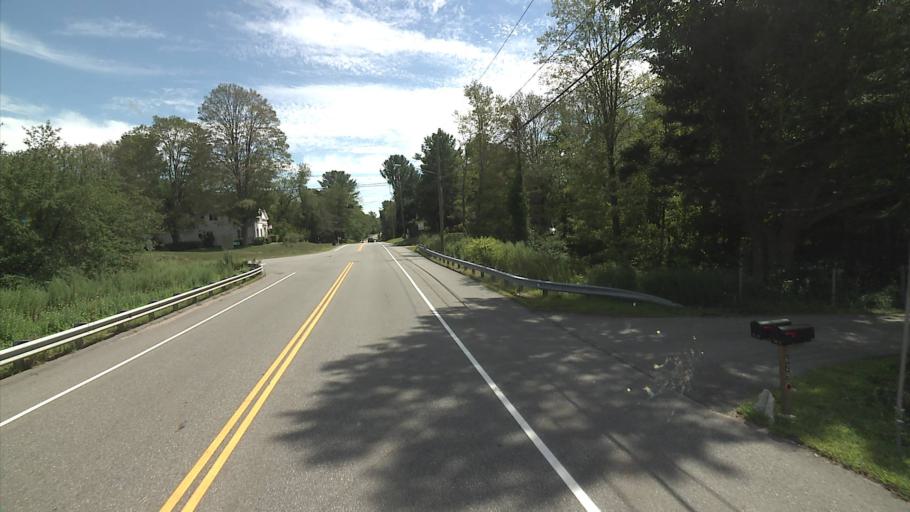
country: US
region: Connecticut
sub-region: Tolland County
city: Mansfield City
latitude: 41.7708
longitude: -72.2034
